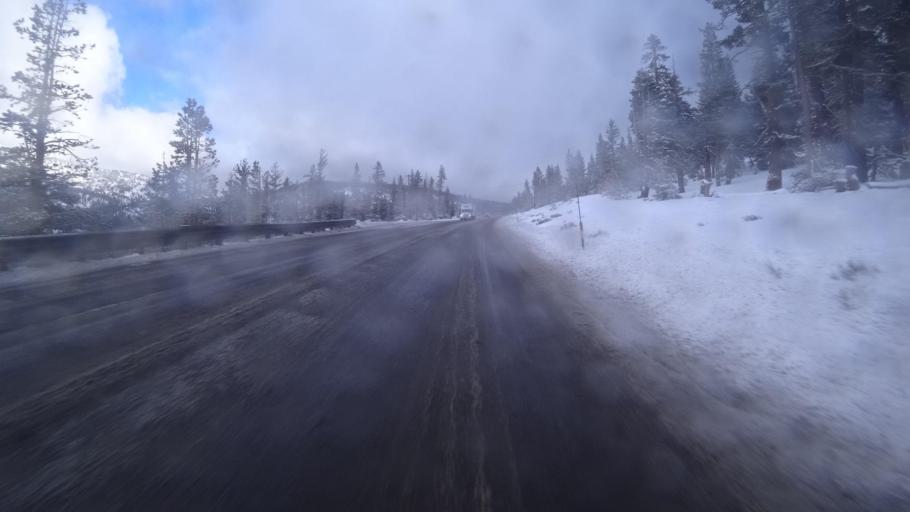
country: US
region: Nevada
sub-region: Washoe County
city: Incline Village
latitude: 39.2926
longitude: -119.9259
